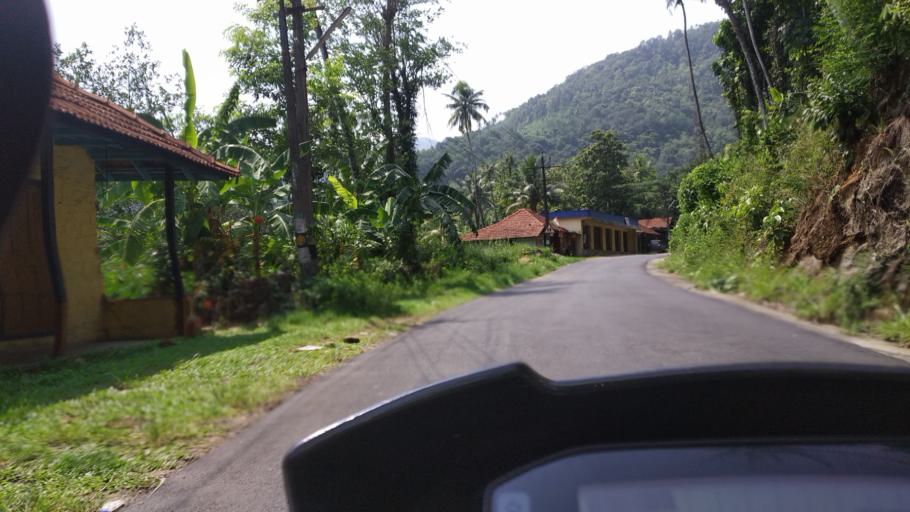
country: IN
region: Kerala
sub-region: Kottayam
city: Erattupetta
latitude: 9.6913
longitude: 76.8438
